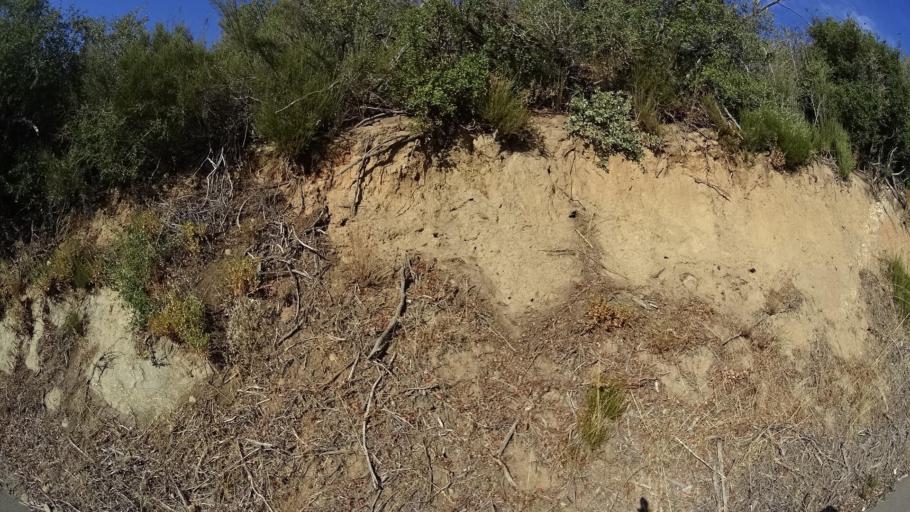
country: US
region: California
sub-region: Riverside County
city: Aguanga
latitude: 33.2634
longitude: -116.7662
